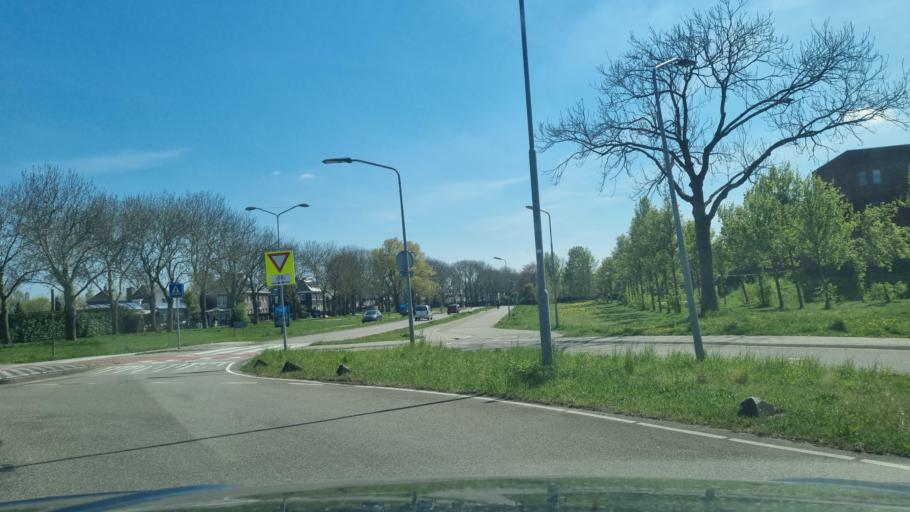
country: NL
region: North Brabant
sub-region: Gemeente 's-Hertogenbosch
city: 's-Hertogenbosch
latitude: 51.7256
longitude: 5.3593
